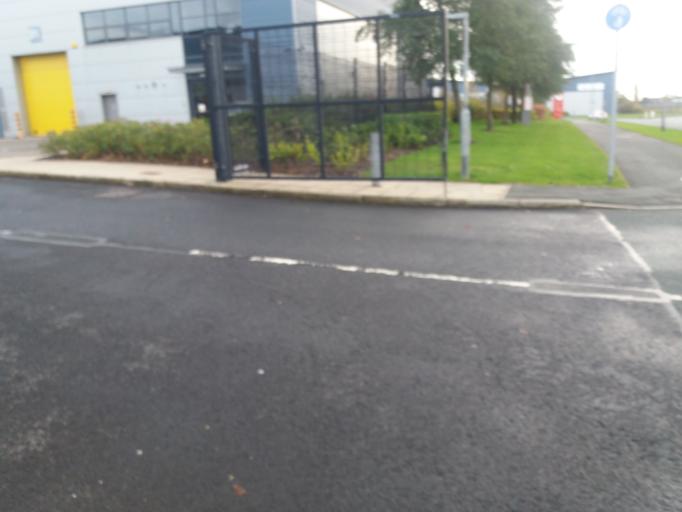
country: GB
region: England
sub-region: Lancashire
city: Euxton
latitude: 53.6754
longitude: -2.6572
